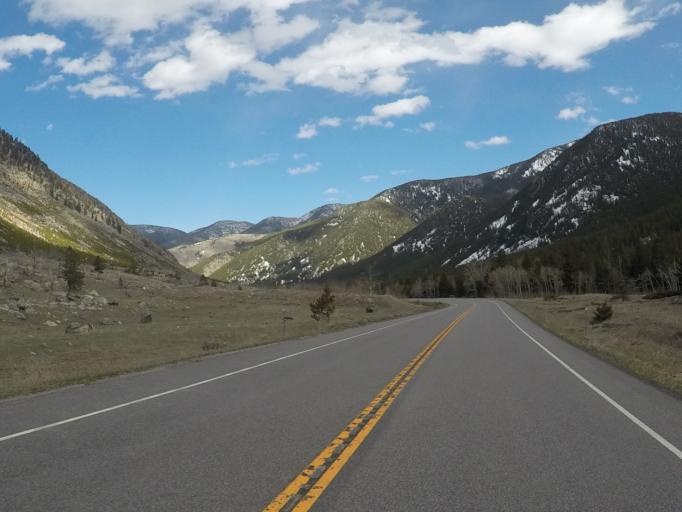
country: US
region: Montana
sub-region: Carbon County
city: Red Lodge
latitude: 45.0873
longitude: -109.3543
